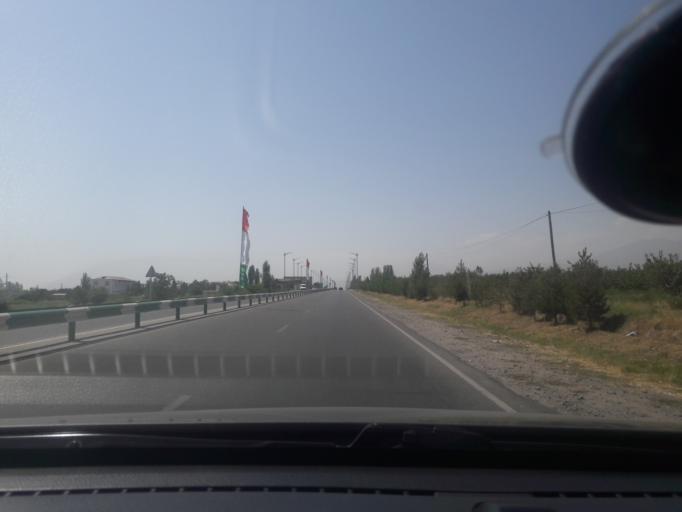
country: TJ
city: Shahrinav
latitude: 38.5617
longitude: 68.4261
